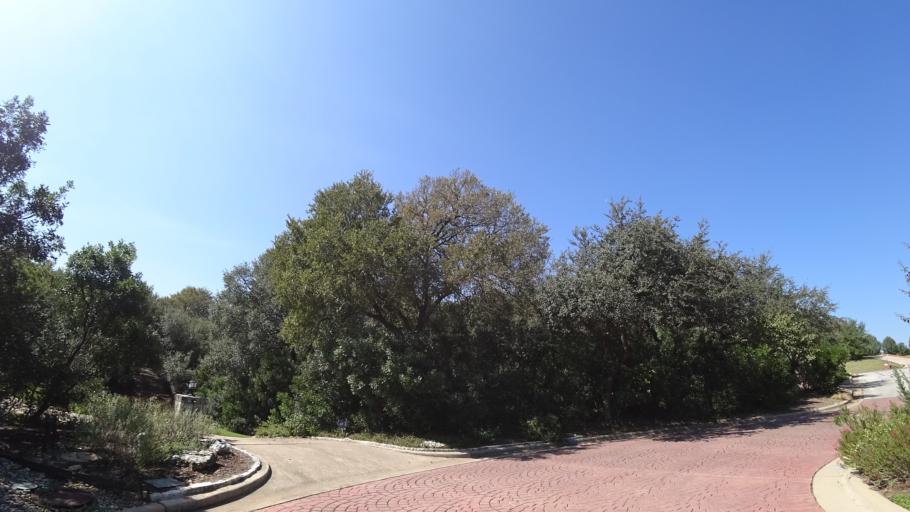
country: US
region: Texas
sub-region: Travis County
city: Rollingwood
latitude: 30.2781
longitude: -97.7953
